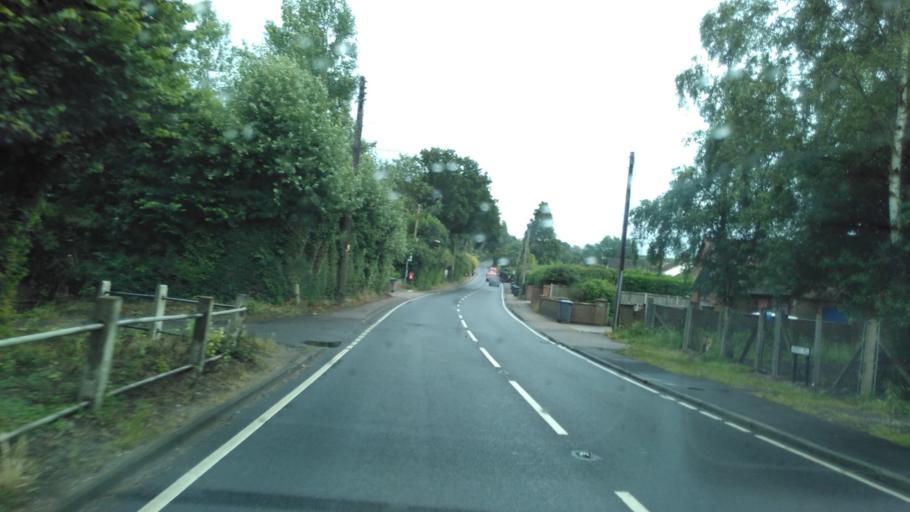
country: GB
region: England
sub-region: Kent
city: Blean
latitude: 51.3195
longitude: 1.0321
